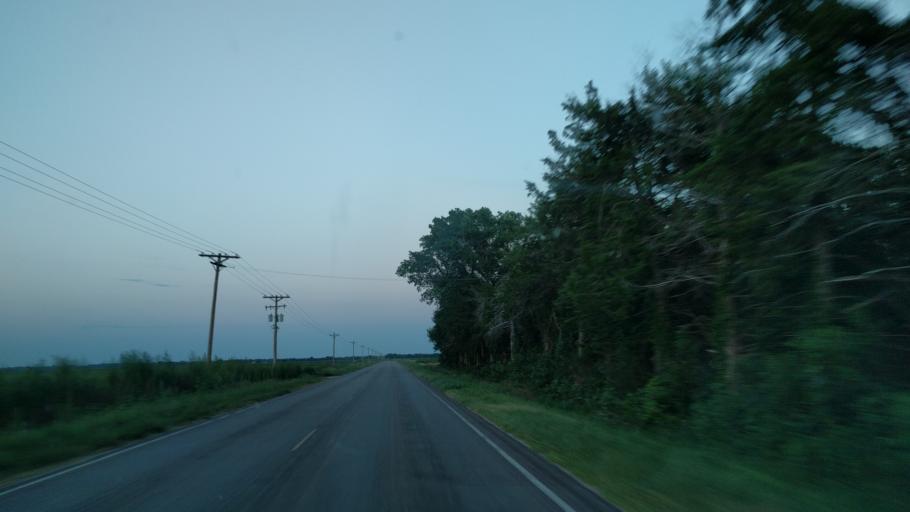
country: US
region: Kansas
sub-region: Reno County
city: Nickerson
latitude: 38.2176
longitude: -98.1043
